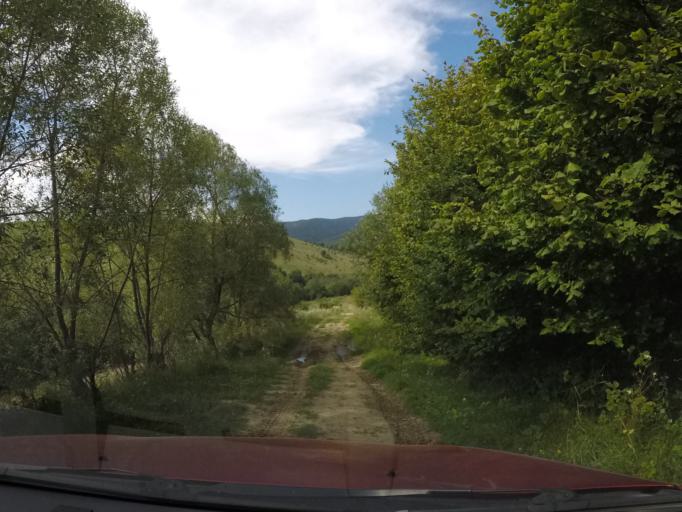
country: UA
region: Zakarpattia
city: Velykyi Bereznyi
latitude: 49.0275
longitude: 22.6369
